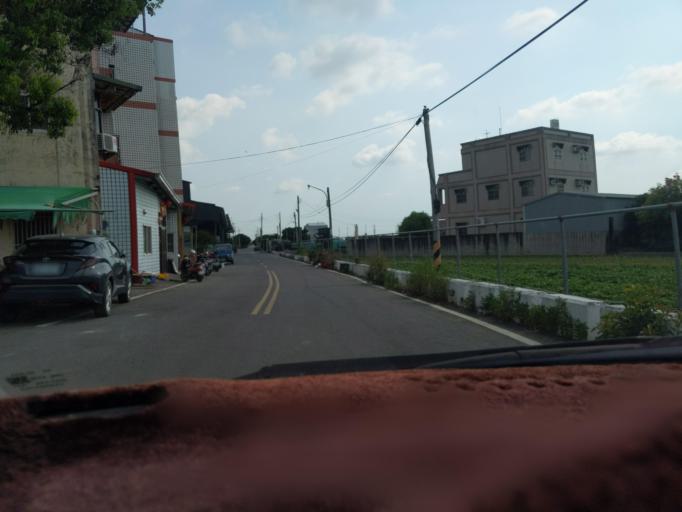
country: TW
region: Taiwan
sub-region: Yunlin
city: Douliu
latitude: 23.7934
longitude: 120.4199
